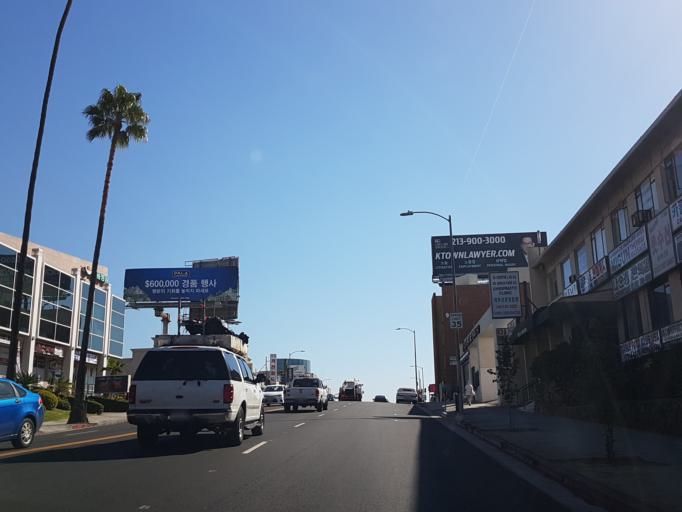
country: US
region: California
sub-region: Los Angeles County
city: Hollywood
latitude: 34.0542
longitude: -118.3092
